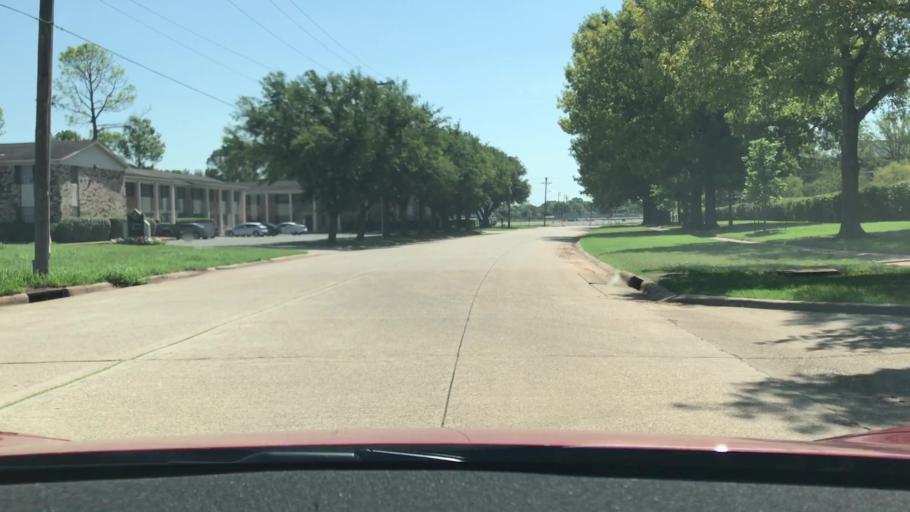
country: US
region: Louisiana
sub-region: Bossier Parish
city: Bossier City
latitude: 32.4491
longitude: -93.7197
